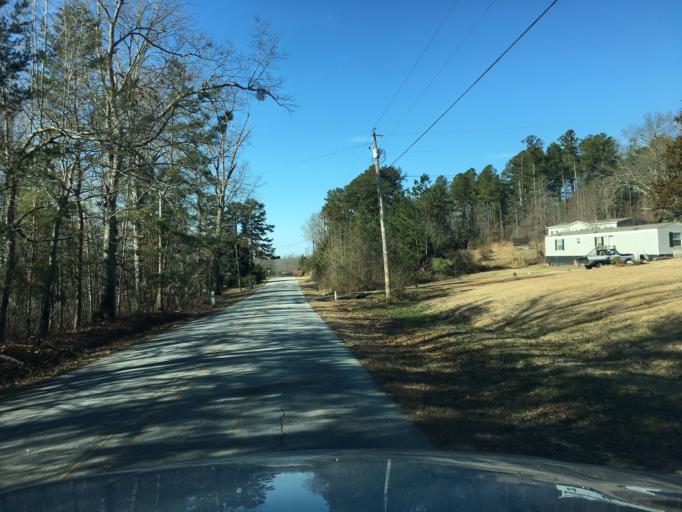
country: US
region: South Carolina
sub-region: Pickens County
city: Arial
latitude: 34.8735
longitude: -82.6582
